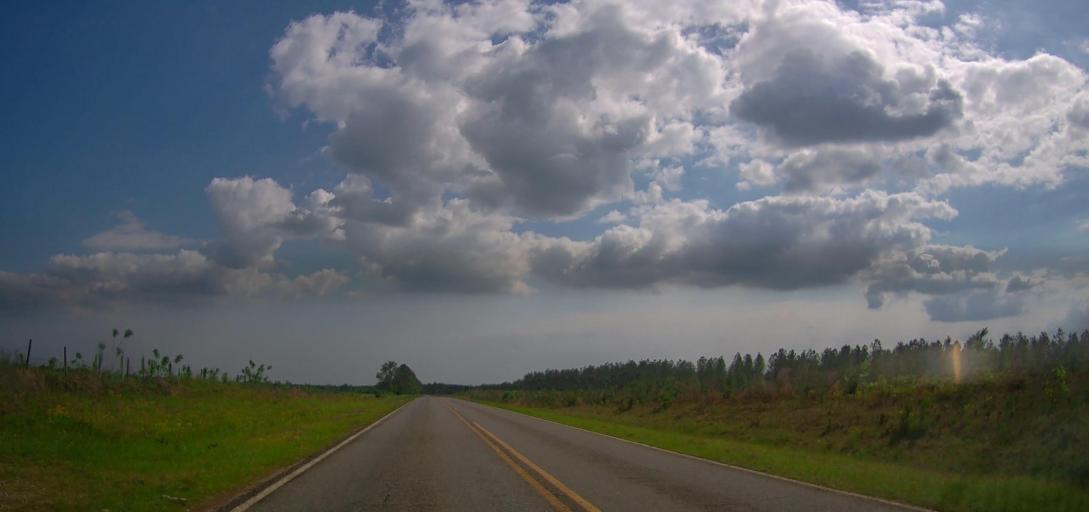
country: US
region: Georgia
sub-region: Laurens County
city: East Dublin
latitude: 32.7190
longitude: -82.9159
